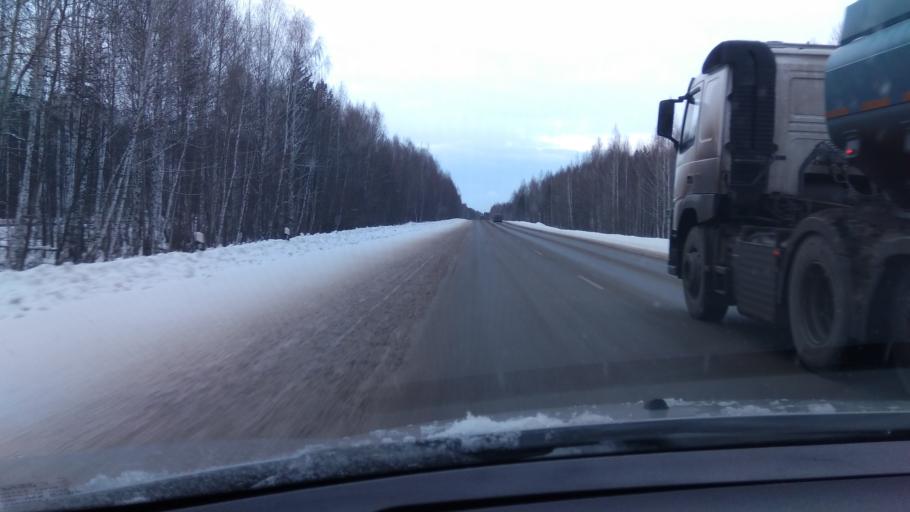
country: RU
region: Sverdlovsk
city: Tsementnyy
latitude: 57.4194
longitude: 60.2100
